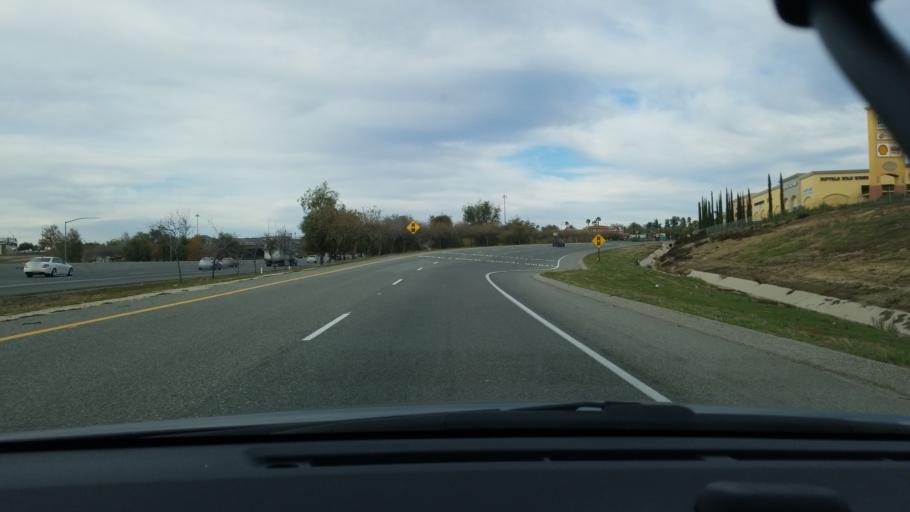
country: US
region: California
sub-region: Riverside County
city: Murrieta Hot Springs
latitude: 33.5531
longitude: -117.1805
